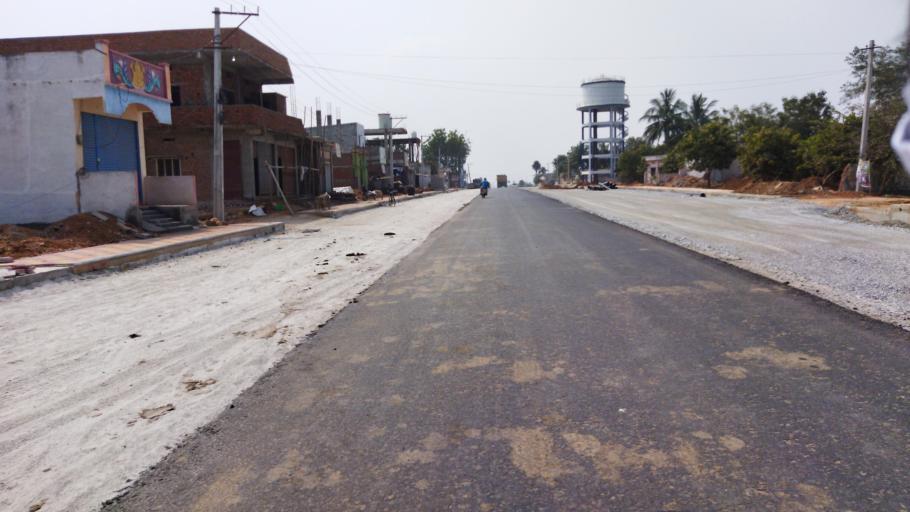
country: IN
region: Telangana
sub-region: Nalgonda
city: Nalgonda
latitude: 17.0913
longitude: 79.3301
